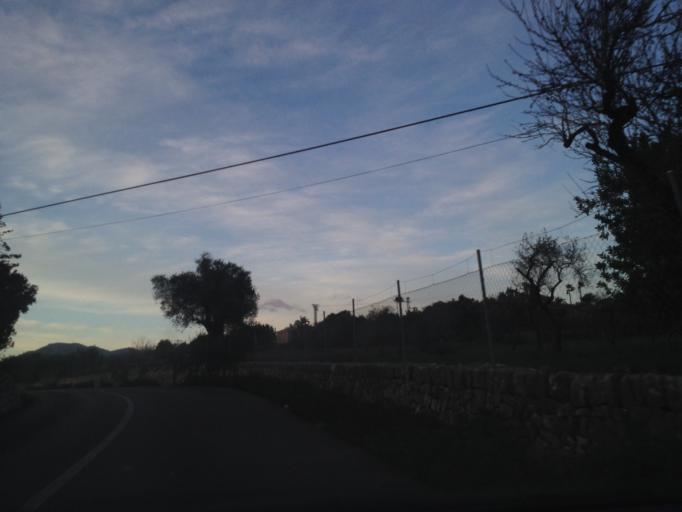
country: ES
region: Balearic Islands
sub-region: Illes Balears
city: Pollenca
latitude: 39.8620
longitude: 3.0468
